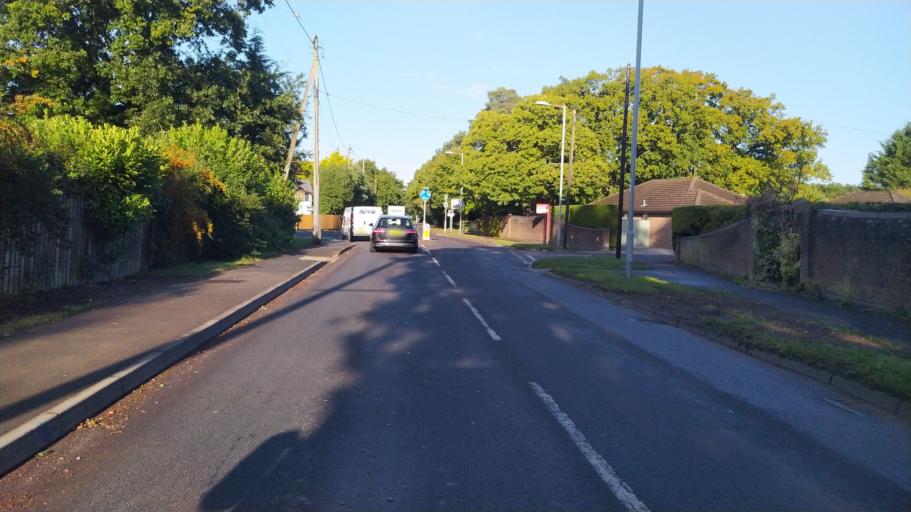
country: GB
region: England
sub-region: Dorset
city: Three Legged Cross
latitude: 50.8505
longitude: -1.8872
